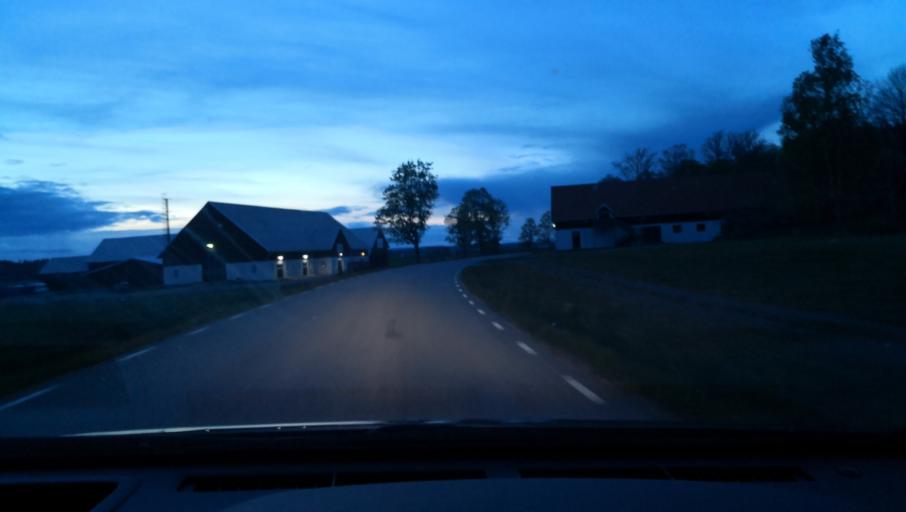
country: SE
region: OErebro
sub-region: Orebro Kommun
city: Vintrosa
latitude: 59.1343
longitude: 14.9984
